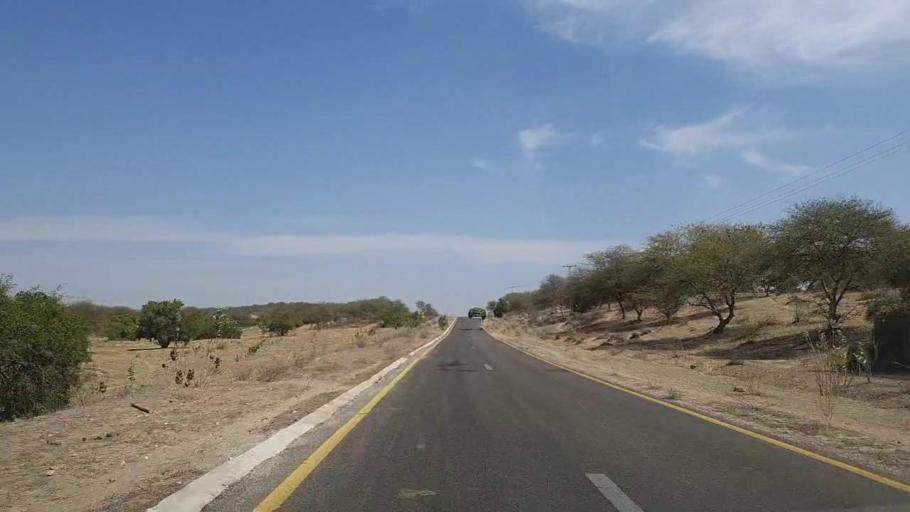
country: PK
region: Sindh
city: Mithi
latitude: 24.8674
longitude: 69.8467
